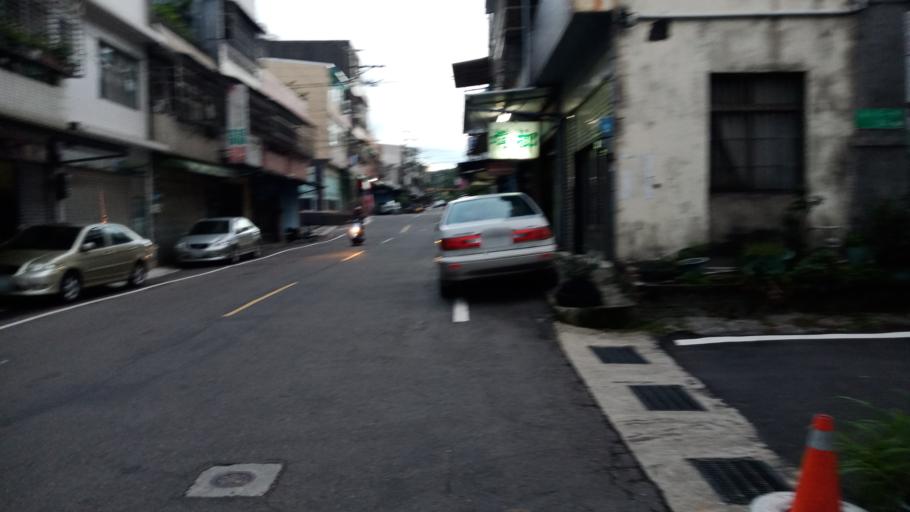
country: TW
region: Taiwan
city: Daxi
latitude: 24.8725
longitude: 121.1986
